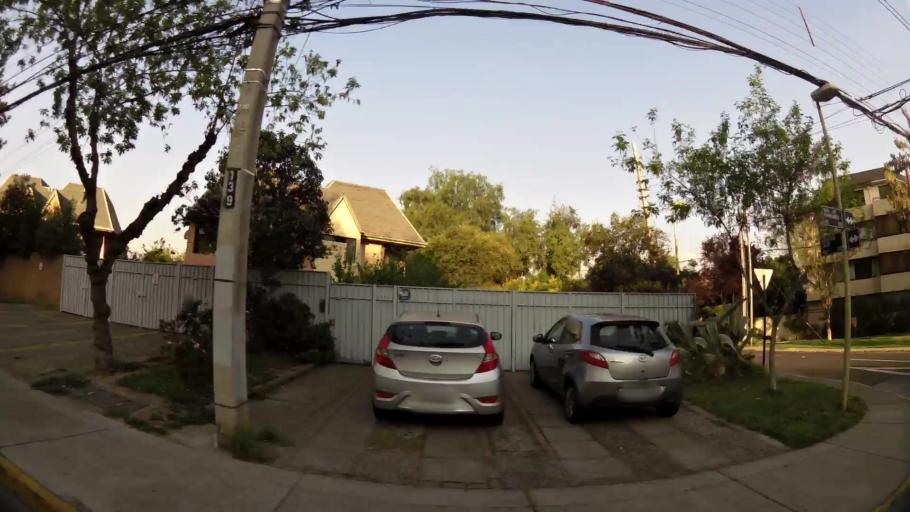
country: CL
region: Santiago Metropolitan
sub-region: Provincia de Santiago
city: Villa Presidente Frei, Nunoa, Santiago, Chile
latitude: -33.3932
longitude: -70.5535
